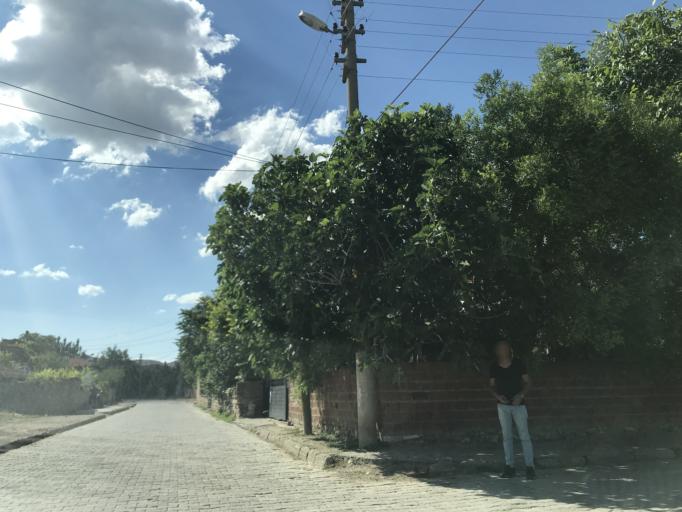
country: TR
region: Denizli
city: Civril
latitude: 38.3040
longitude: 29.7426
